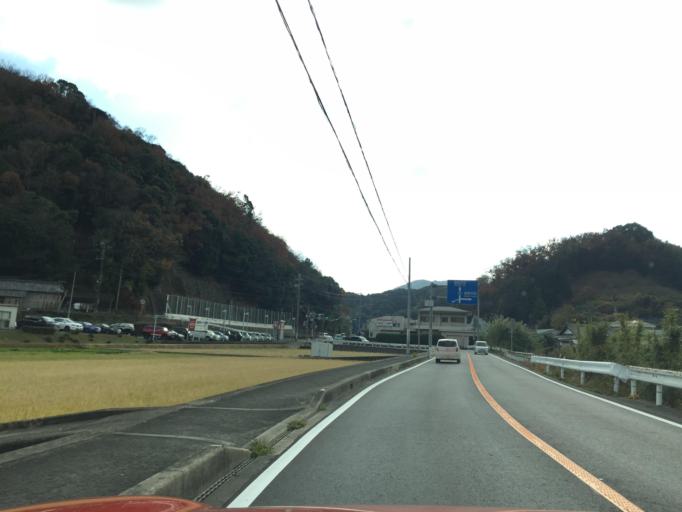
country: JP
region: Wakayama
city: Kainan
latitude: 34.1671
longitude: 135.2509
